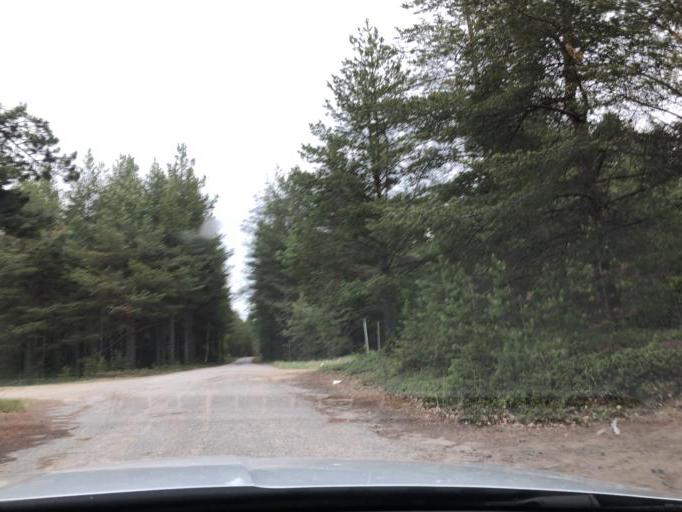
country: SE
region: Norrbotten
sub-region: Pitea Kommun
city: Pitea
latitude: 65.2349
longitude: 21.5139
